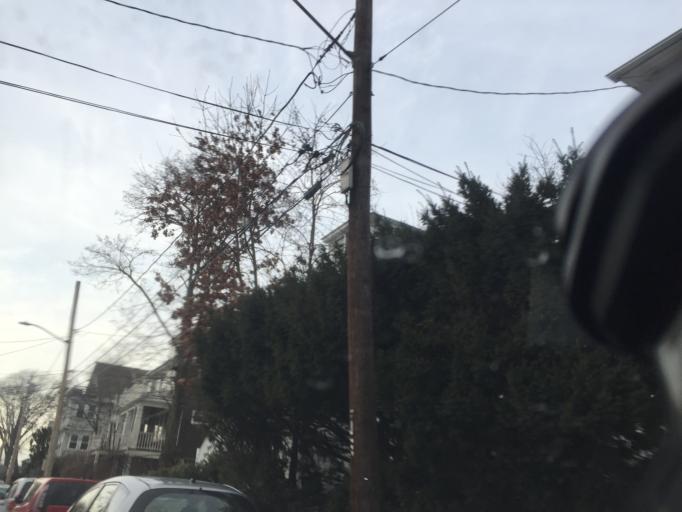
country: US
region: Massachusetts
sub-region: Middlesex County
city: Watertown
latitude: 42.3476
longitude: -71.1663
